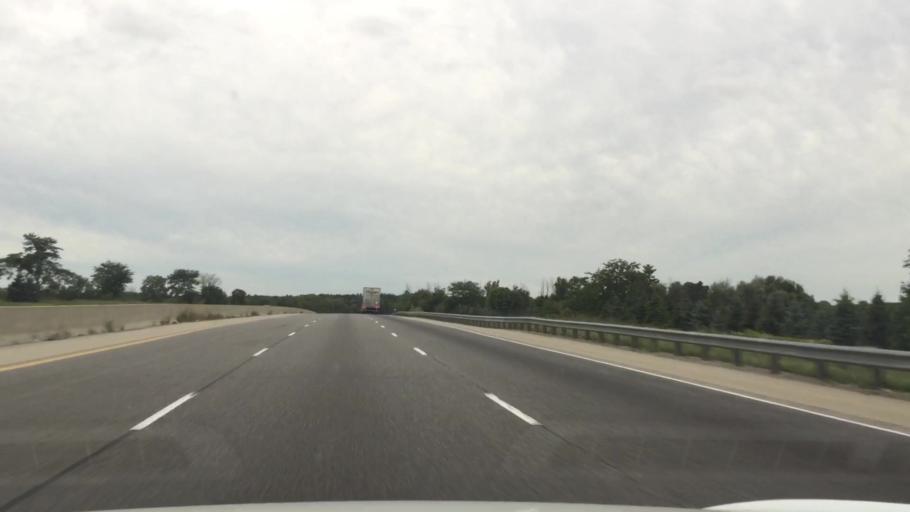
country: CA
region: Ontario
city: Kitchener
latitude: 43.2783
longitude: -80.5235
